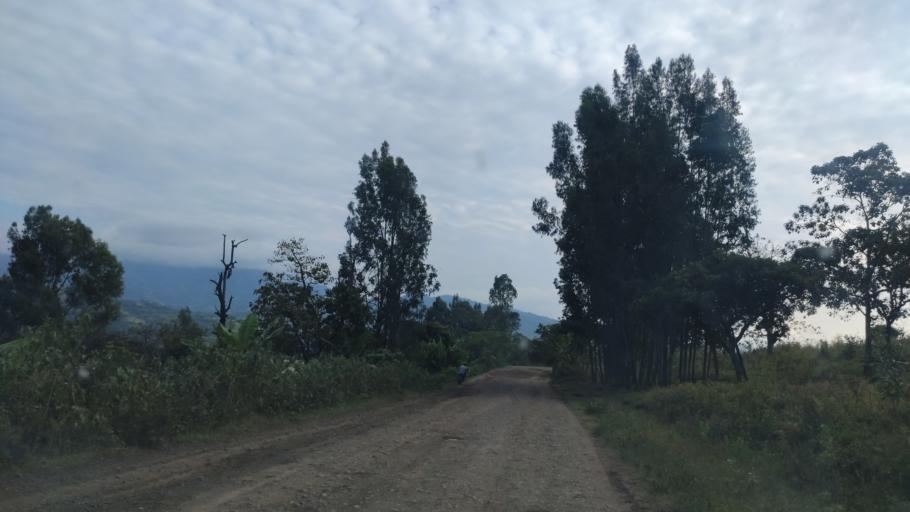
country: ET
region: Southern Nations, Nationalities, and People's Region
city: Arba Minch'
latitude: 6.4413
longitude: 37.3917
